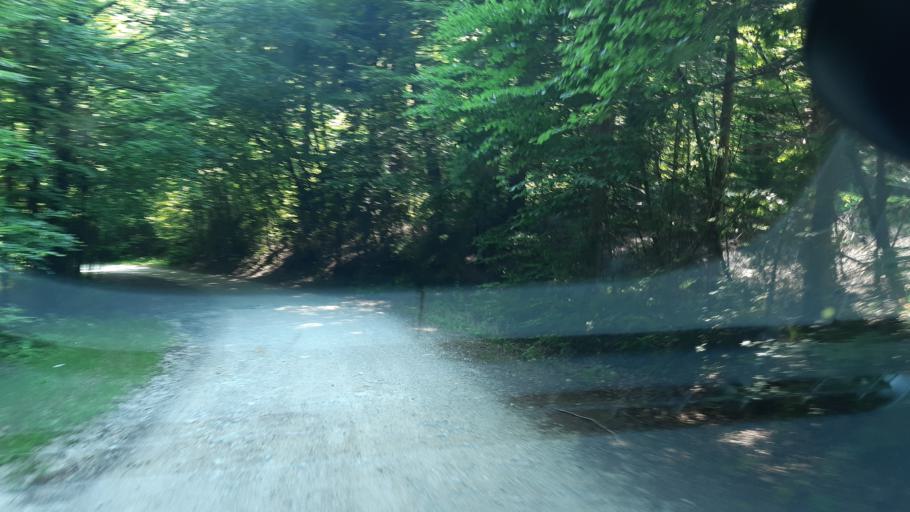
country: SI
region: Trzic
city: Bistrica pri Trzicu
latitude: 46.3747
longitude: 14.2741
